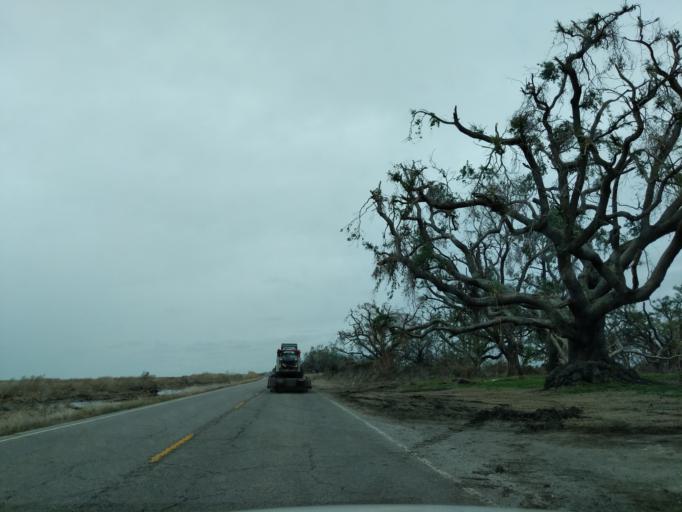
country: US
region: Louisiana
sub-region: Cameron Parish
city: Cameron
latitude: 29.7836
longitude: -93.0864
